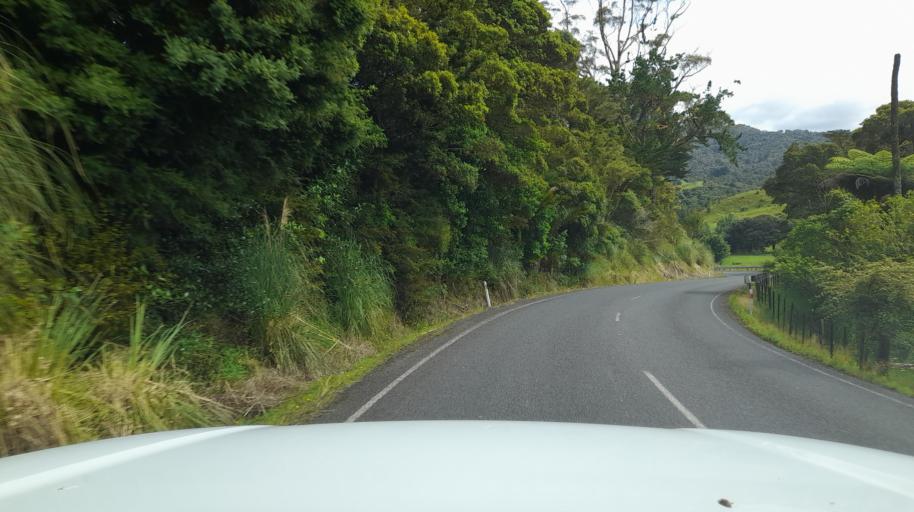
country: NZ
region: Northland
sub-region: Far North District
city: Kaitaia
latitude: -35.2674
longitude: 173.4183
